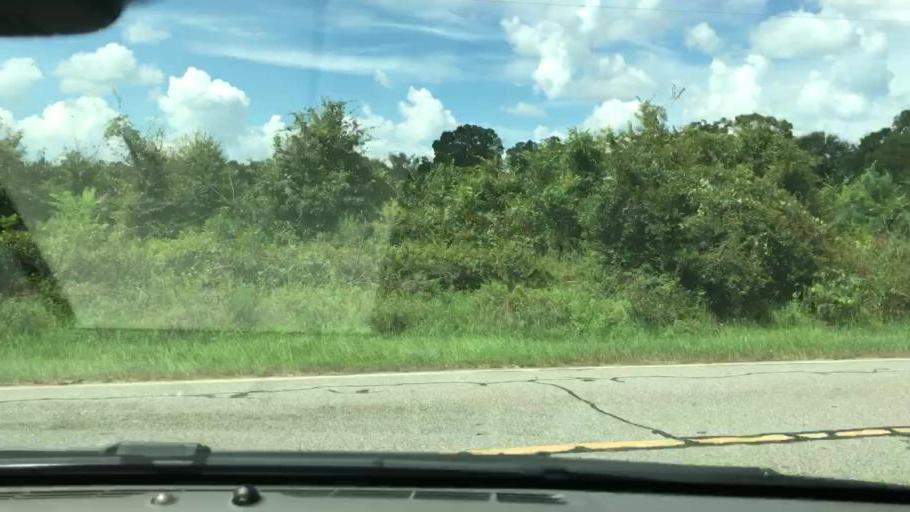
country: US
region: Georgia
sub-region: Quitman County
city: Georgetown
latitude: 31.9941
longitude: -85.0435
